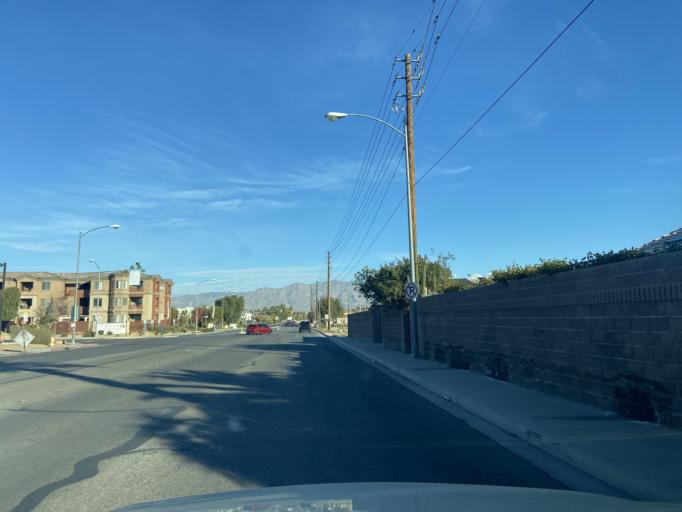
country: US
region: Nevada
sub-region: Clark County
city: Las Vegas
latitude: 36.2371
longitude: -115.1893
